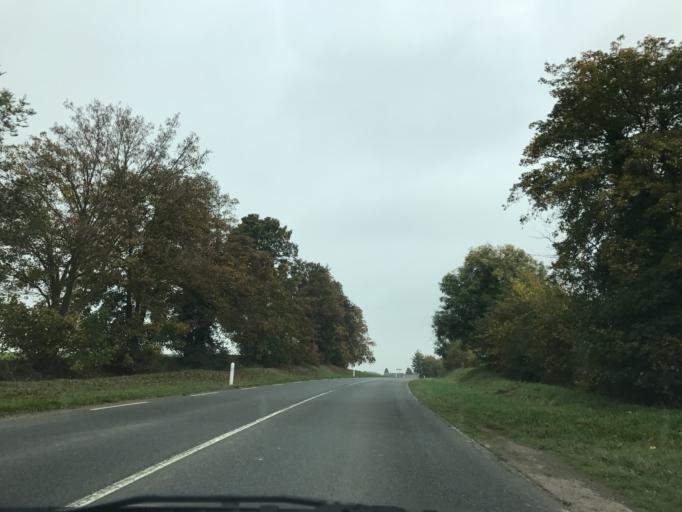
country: FR
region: Picardie
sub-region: Departement de la Somme
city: Peronne
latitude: 49.9001
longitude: 2.9234
